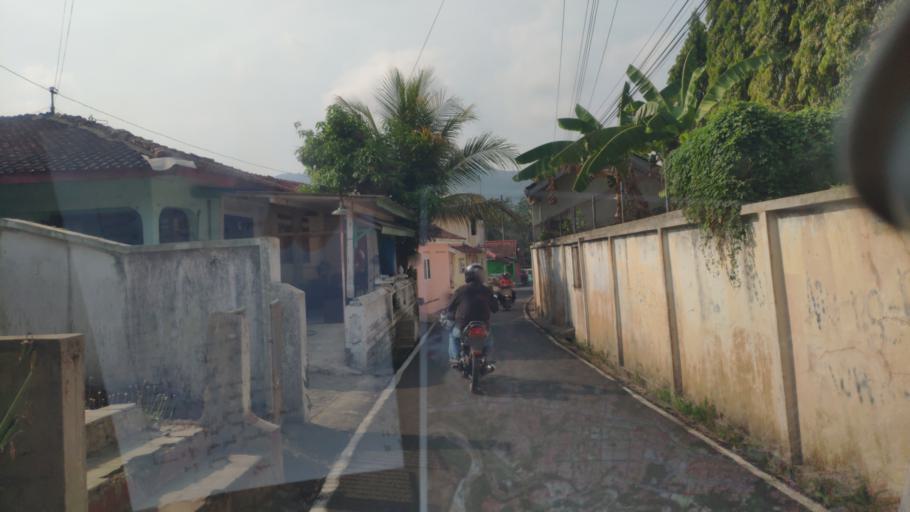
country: ID
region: Central Java
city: Wonosobo
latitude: -7.3983
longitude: 109.6948
